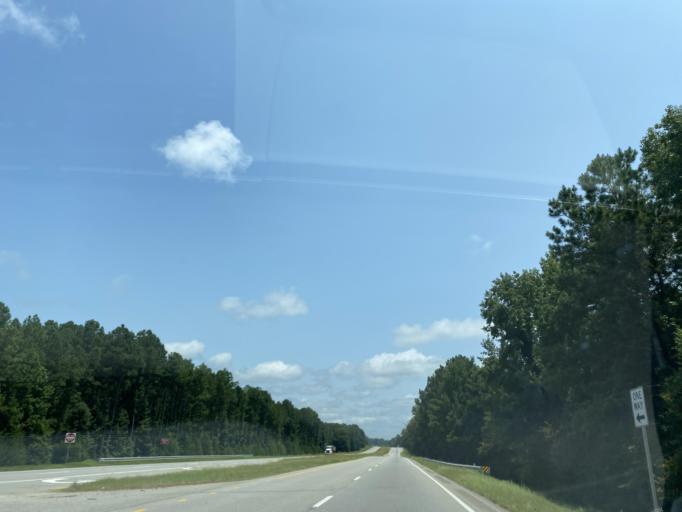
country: US
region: Georgia
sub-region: Telfair County
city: Lumber City
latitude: 31.9064
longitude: -82.6609
